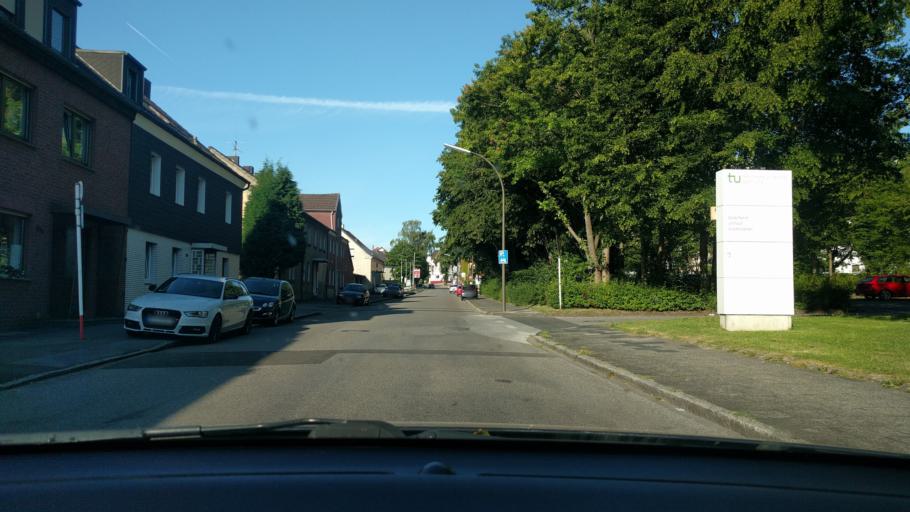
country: DE
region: North Rhine-Westphalia
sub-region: Regierungsbezirk Arnsberg
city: Dortmund
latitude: 51.4824
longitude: 7.4124
